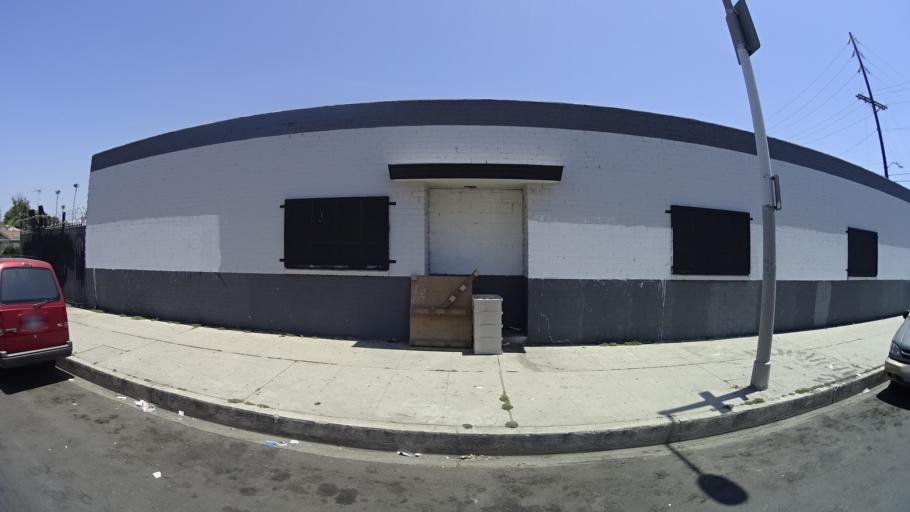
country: US
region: California
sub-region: Los Angeles County
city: Van Nuys
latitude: 34.2141
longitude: -118.4553
